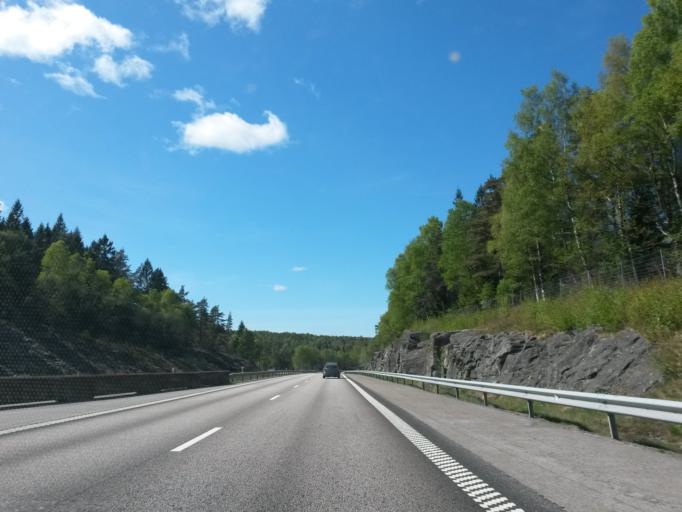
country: SE
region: Vaestra Goetaland
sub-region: Partille Kommun
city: Furulund
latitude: 57.7409
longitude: 12.1823
